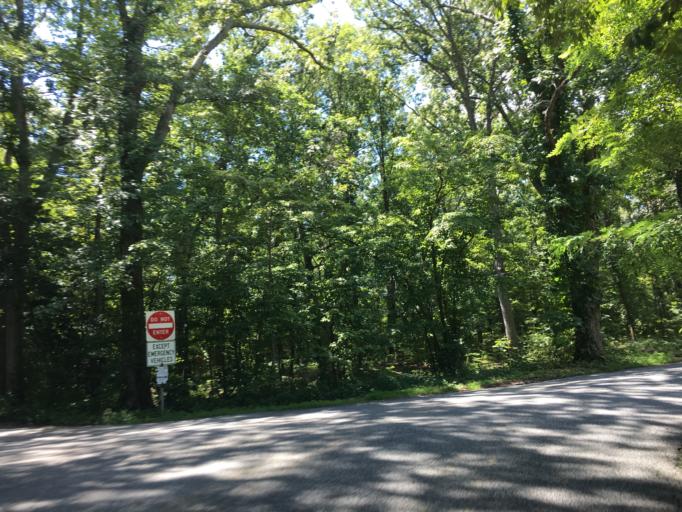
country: US
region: Maryland
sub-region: Anne Arundel County
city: Severna Park
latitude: 39.0869
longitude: -76.5607
